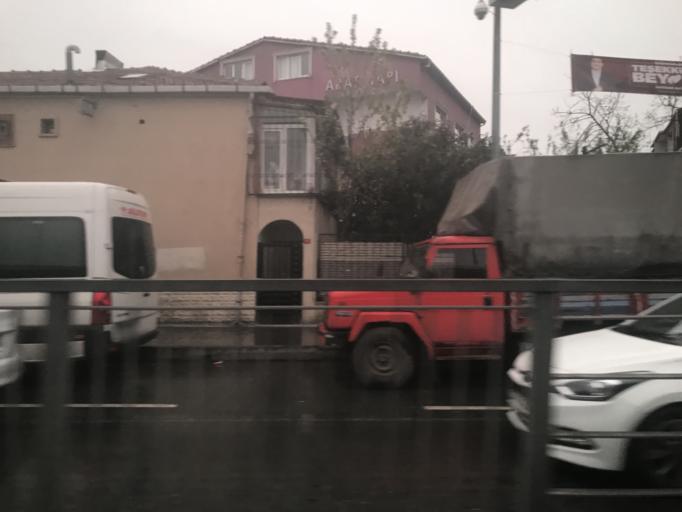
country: TR
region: Istanbul
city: Sisli
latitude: 41.0533
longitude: 28.9579
